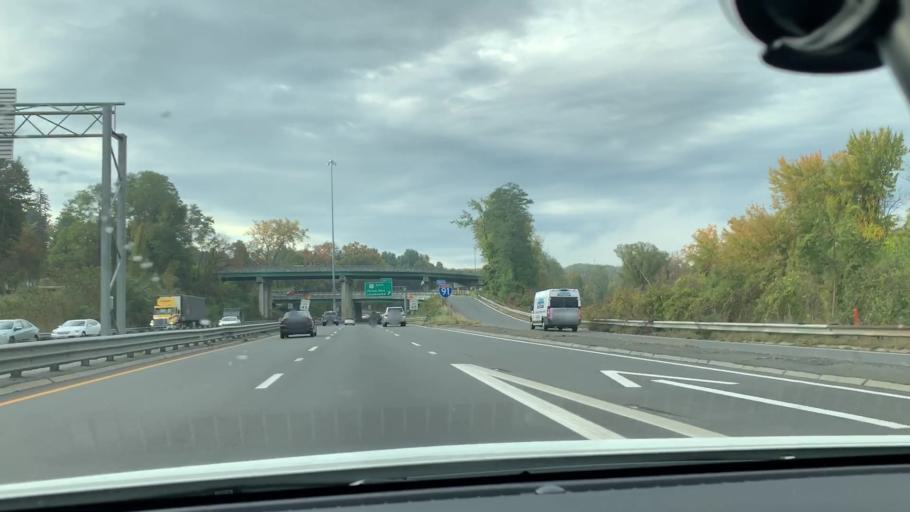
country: US
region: Massachusetts
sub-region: Hampden County
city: Springfield
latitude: 42.0794
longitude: -72.5796
